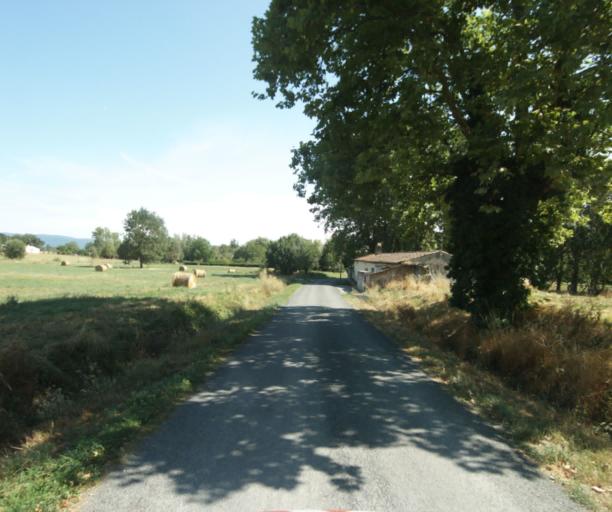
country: FR
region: Midi-Pyrenees
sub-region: Departement de la Haute-Garonne
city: Revel
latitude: 43.4964
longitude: 1.9693
